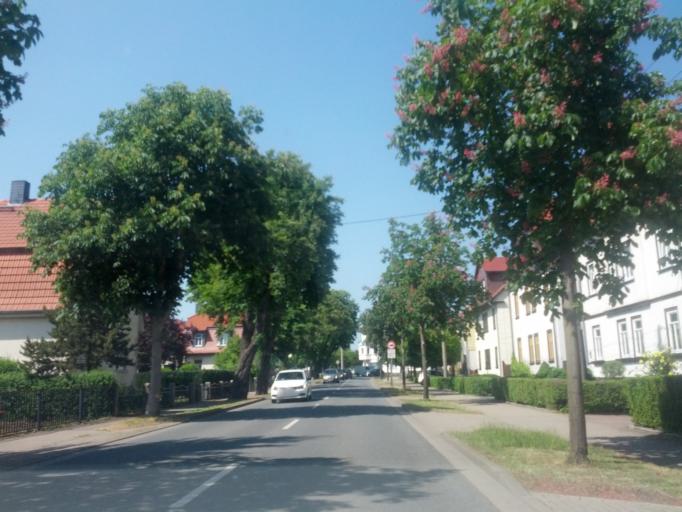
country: DE
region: Thuringia
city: Gotha
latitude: 50.9430
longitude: 10.7389
